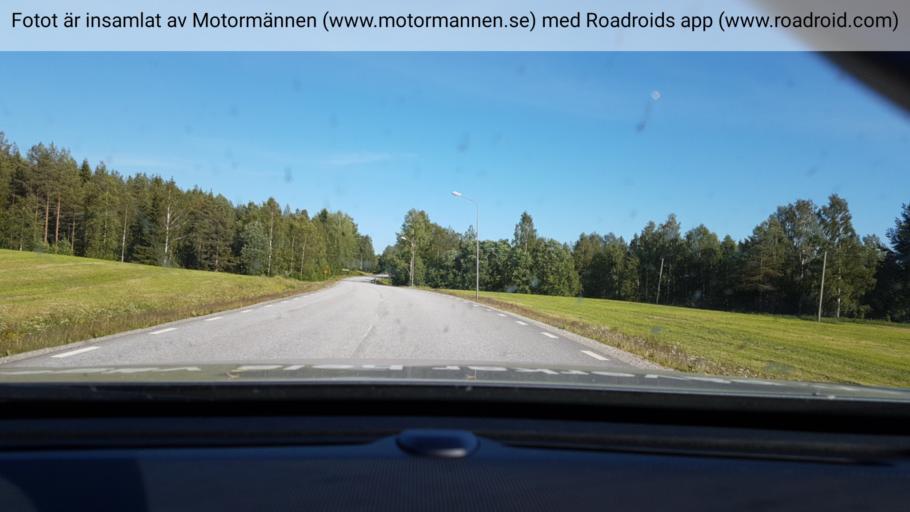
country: SE
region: Vaesterbotten
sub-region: Vindelns Kommun
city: Vindeln
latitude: 64.1303
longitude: 19.5388
